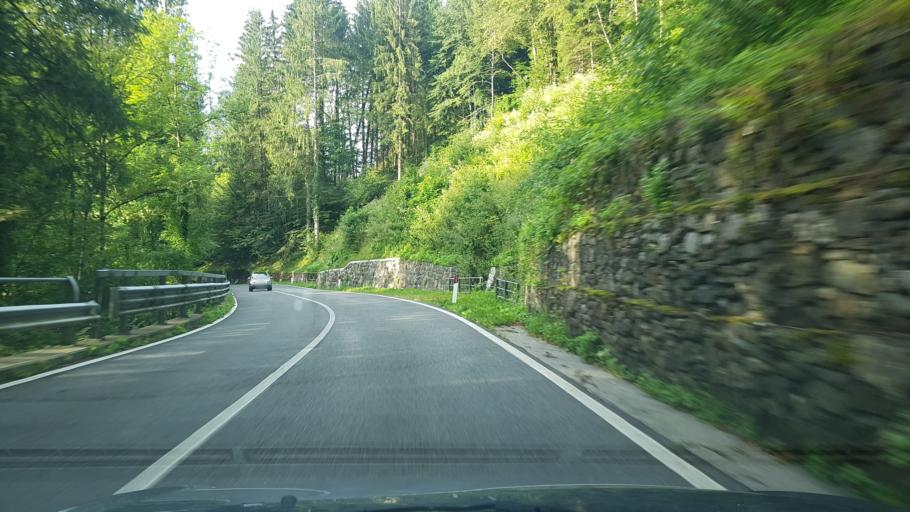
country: IT
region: Friuli Venezia Giulia
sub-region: Provincia di Udine
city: Comeglians
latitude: 46.5249
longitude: 12.8696
